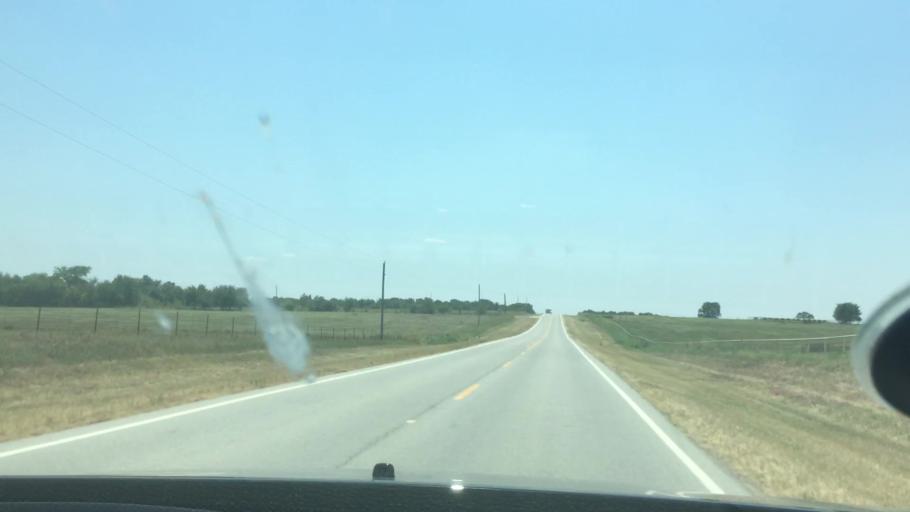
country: US
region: Oklahoma
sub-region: Coal County
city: Coalgate
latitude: 34.5662
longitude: -96.4069
